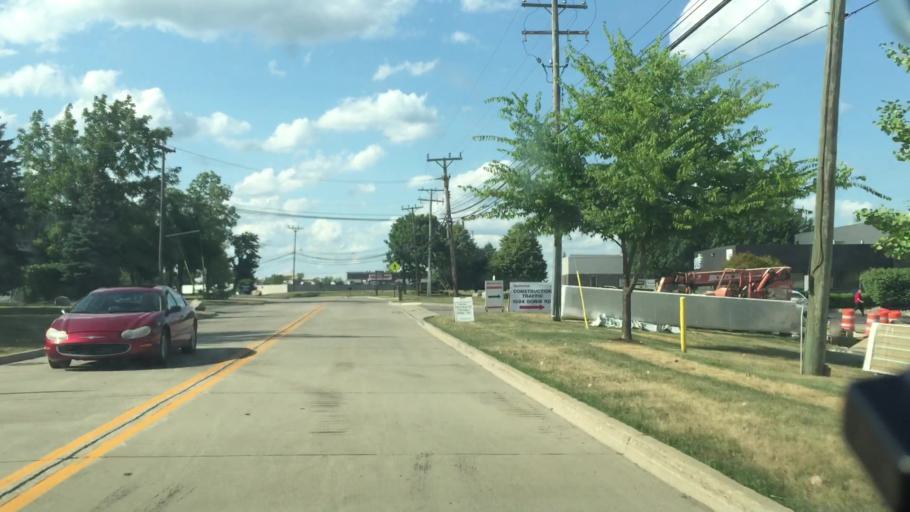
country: US
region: Michigan
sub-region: Oakland County
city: Auburn Hills
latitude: 42.6554
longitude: -83.2432
